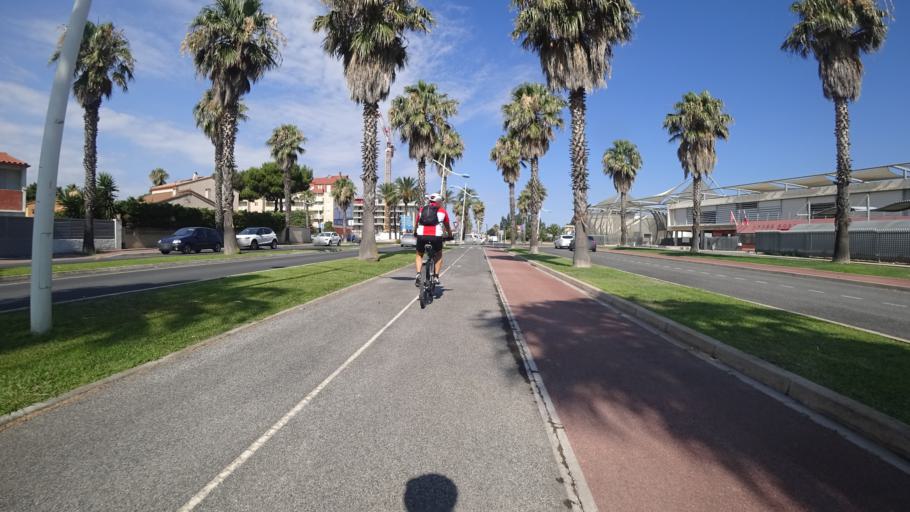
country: FR
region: Languedoc-Roussillon
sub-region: Departement des Pyrenees-Orientales
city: Canet-en-Roussillon
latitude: 42.7019
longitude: 3.0286
